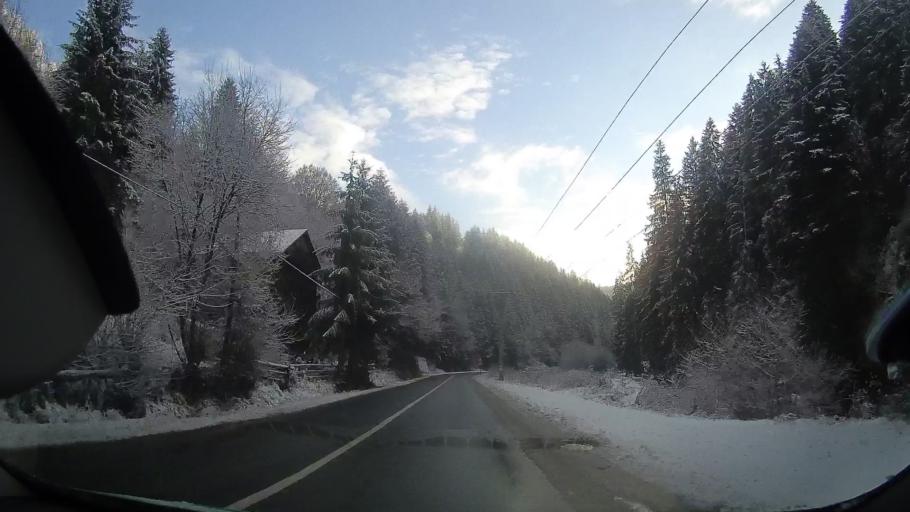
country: RO
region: Alba
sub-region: Comuna Scarisoara
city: Scarisoara
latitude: 46.4565
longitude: 22.8521
